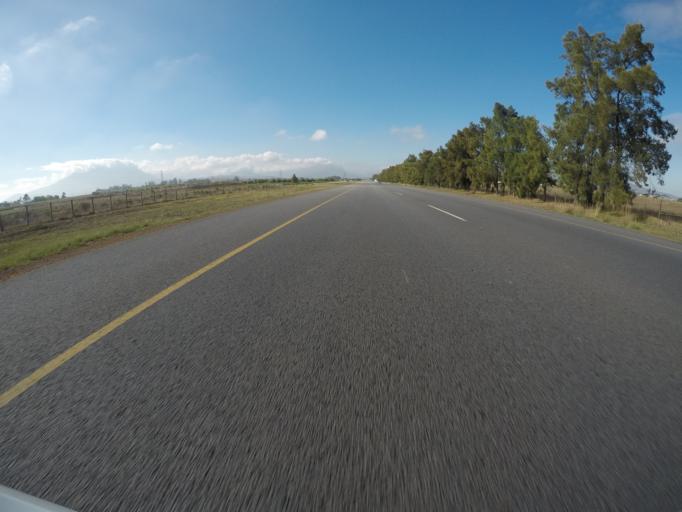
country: ZA
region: Western Cape
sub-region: City of Cape Town
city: Kraaifontein
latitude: -33.8433
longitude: 18.8015
